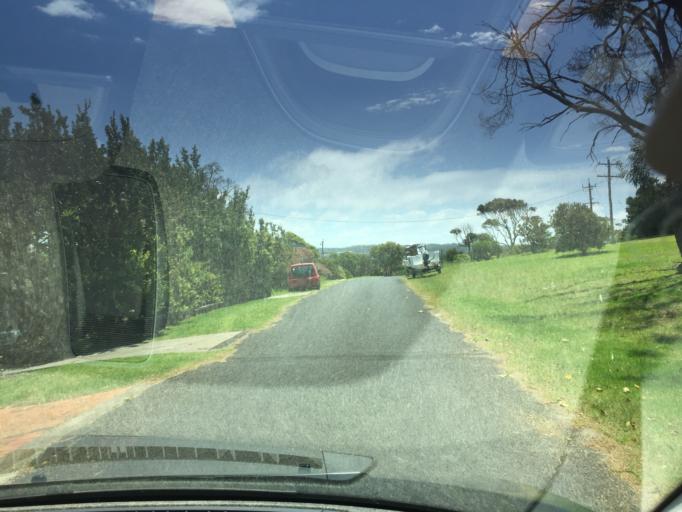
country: AU
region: New South Wales
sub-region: Bega Valley
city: Merimbula
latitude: -36.8949
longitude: 149.9266
